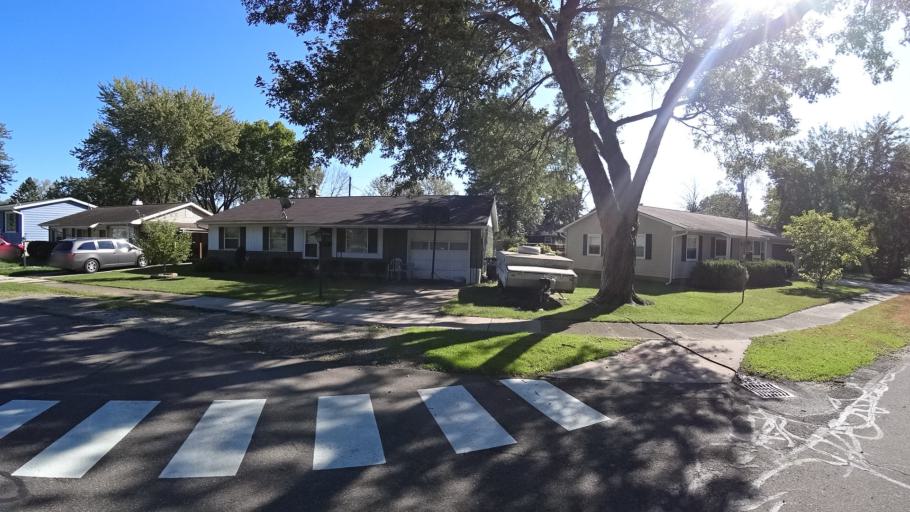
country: US
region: Indiana
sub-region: LaPorte County
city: Michigan City
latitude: 41.6974
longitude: -86.9078
